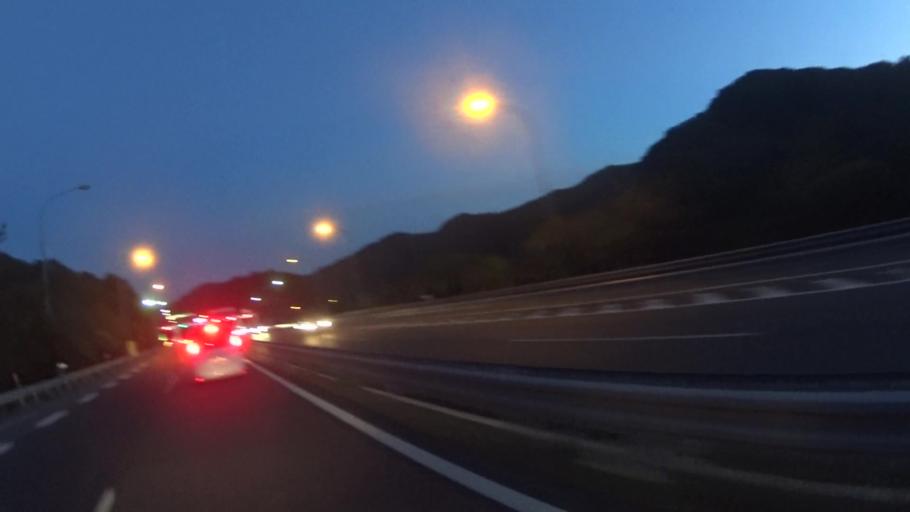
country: JP
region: Kyoto
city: Kameoka
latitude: 35.1058
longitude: 135.4854
